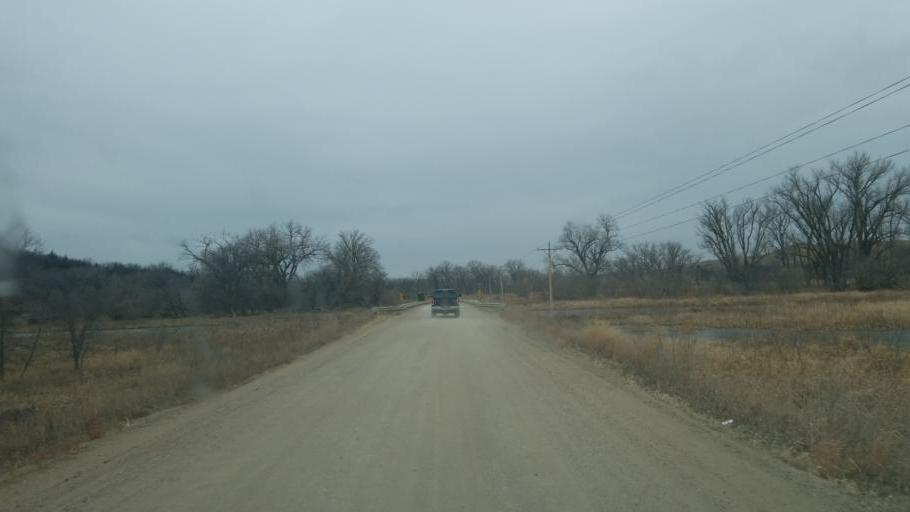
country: US
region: South Dakota
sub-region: Bon Homme County
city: Springfield
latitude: 42.7310
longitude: -97.9214
